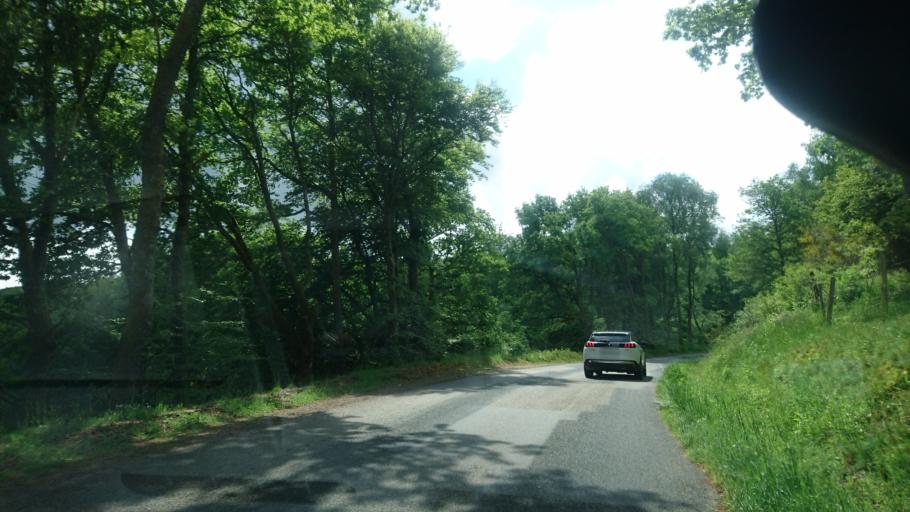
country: FR
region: Limousin
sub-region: Departement de la Haute-Vienne
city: Peyrat-le-Chateau
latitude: 45.7870
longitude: 1.9009
